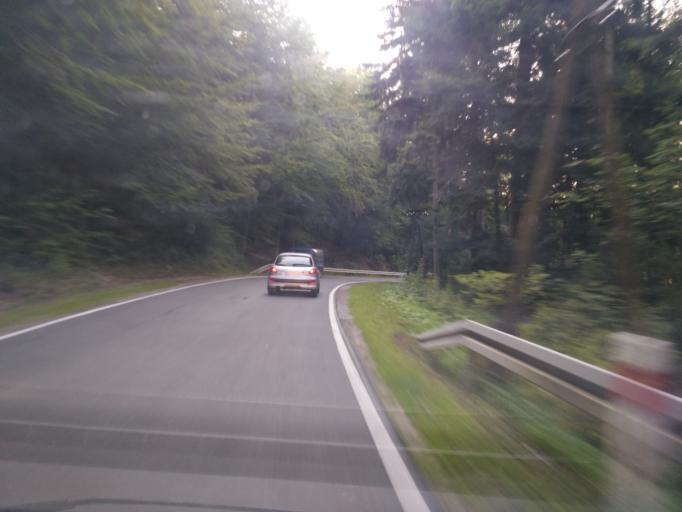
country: PL
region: Subcarpathian Voivodeship
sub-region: Powiat krosnienski
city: Korczyna
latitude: 49.7412
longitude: 21.8073
